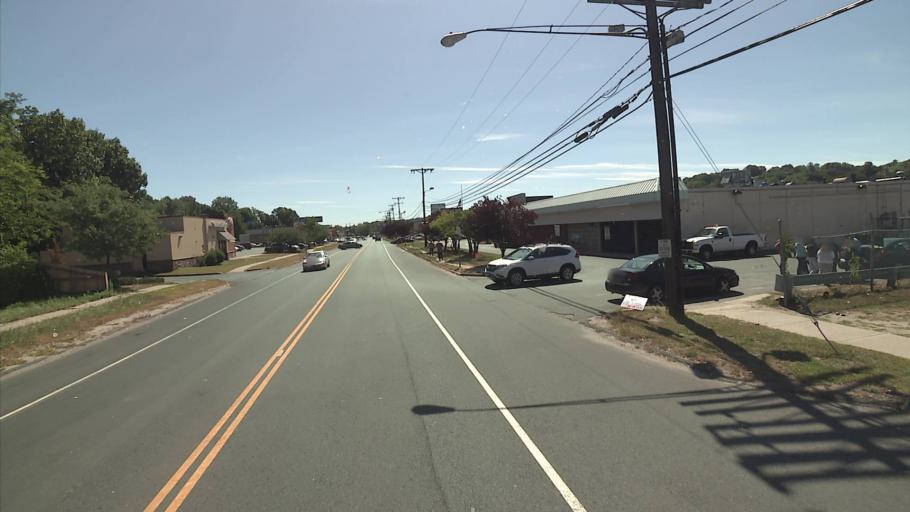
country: US
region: Connecticut
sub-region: New Haven County
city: Waterbury
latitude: 41.5624
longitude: -73.0539
